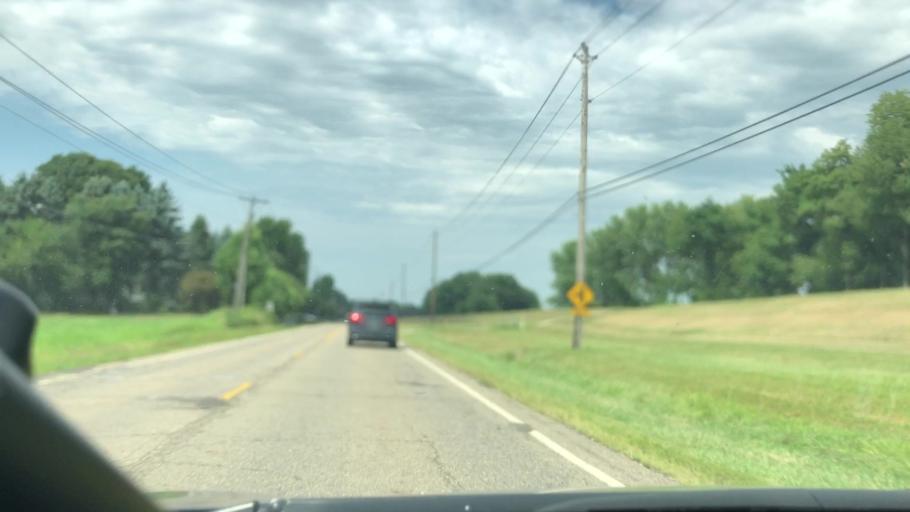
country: US
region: Ohio
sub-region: Summit County
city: New Franklin
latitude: 40.9469
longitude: -81.5340
